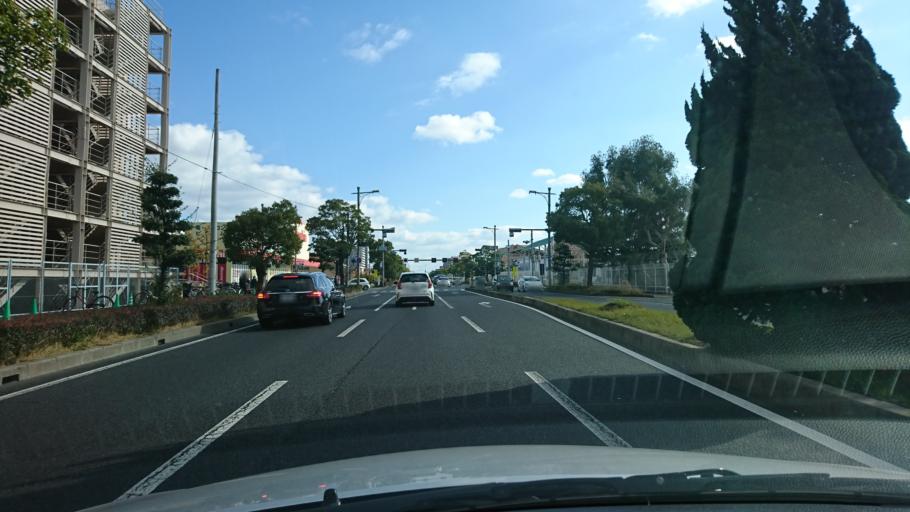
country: JP
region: Hyogo
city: Akashi
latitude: 34.6781
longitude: 134.9344
